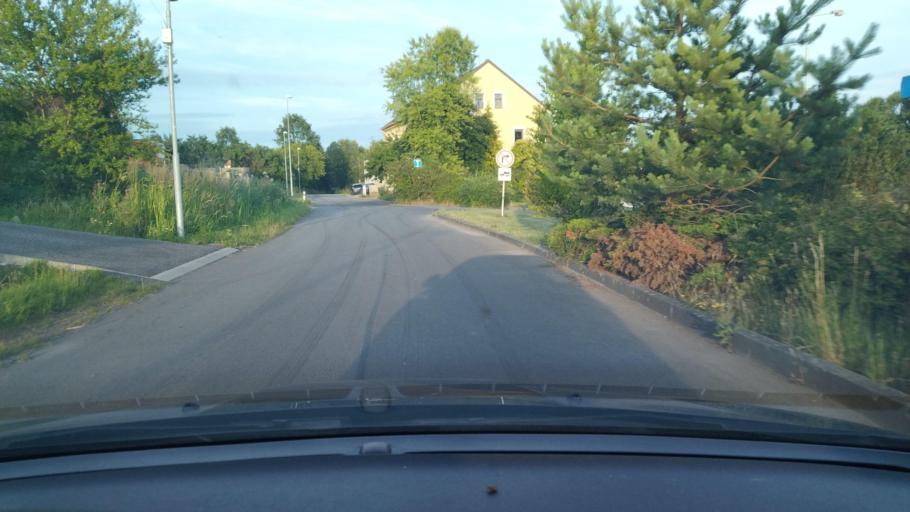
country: CZ
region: Liberecky
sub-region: Okres Ceska Lipa
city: Ceska Lipa
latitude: 50.6822
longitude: 14.5643
